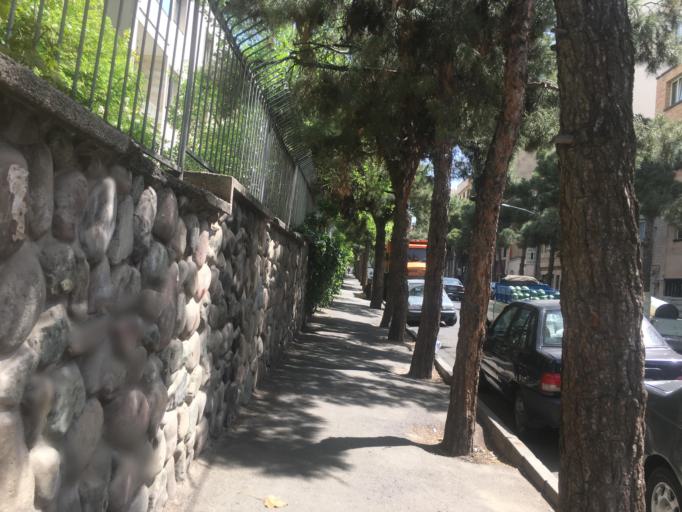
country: IR
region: Tehran
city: Tehran
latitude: 35.7433
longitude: 51.5468
